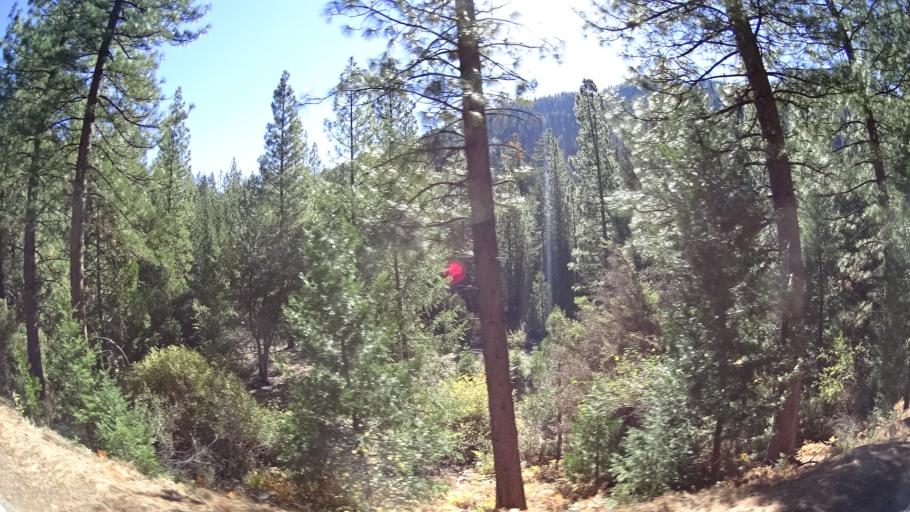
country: US
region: California
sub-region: Trinity County
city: Weaverville
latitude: 41.2264
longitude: -122.9968
